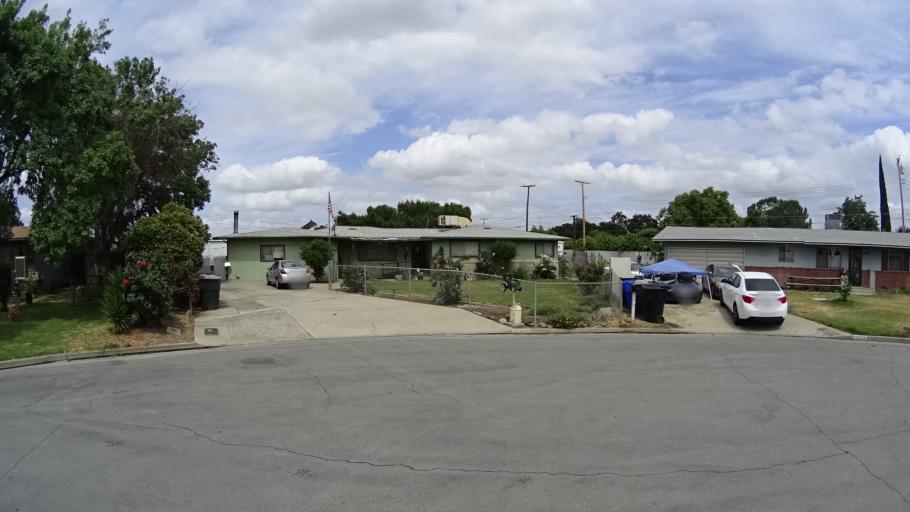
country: US
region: California
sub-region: Kings County
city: Home Garden
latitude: 36.3047
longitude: -119.6609
